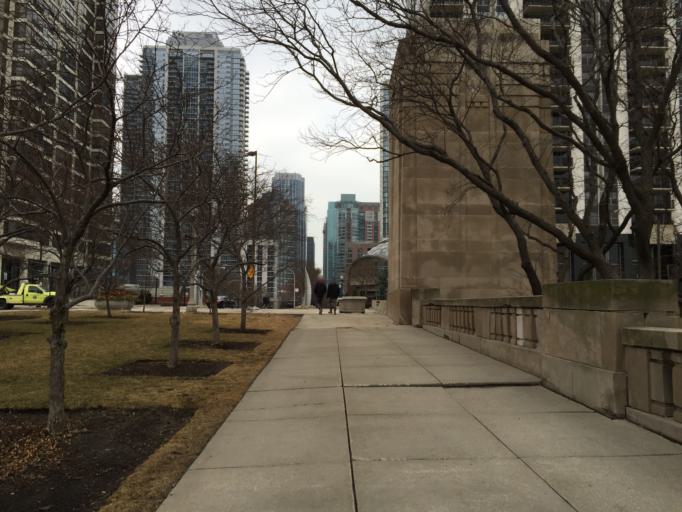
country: US
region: Illinois
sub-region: Cook County
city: Chicago
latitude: 41.8840
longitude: -87.6173
